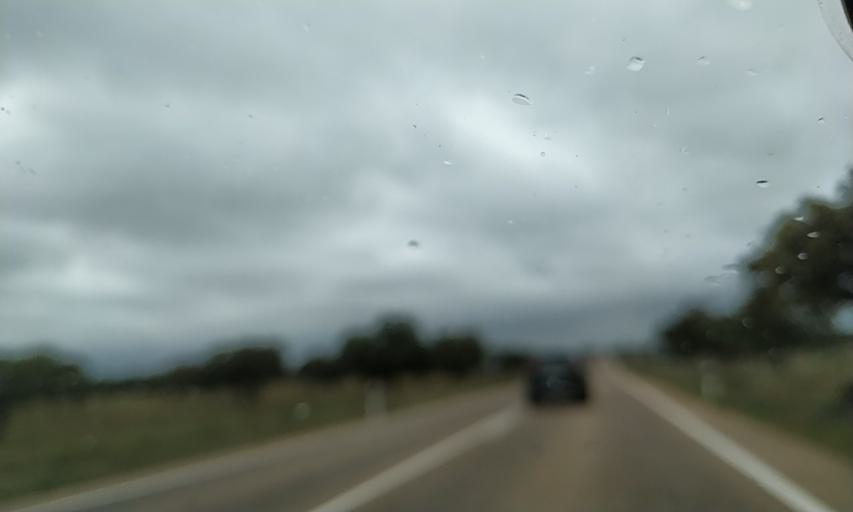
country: ES
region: Extremadura
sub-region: Provincia de Badajoz
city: Villar del Rey
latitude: 39.0006
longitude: -6.8656
